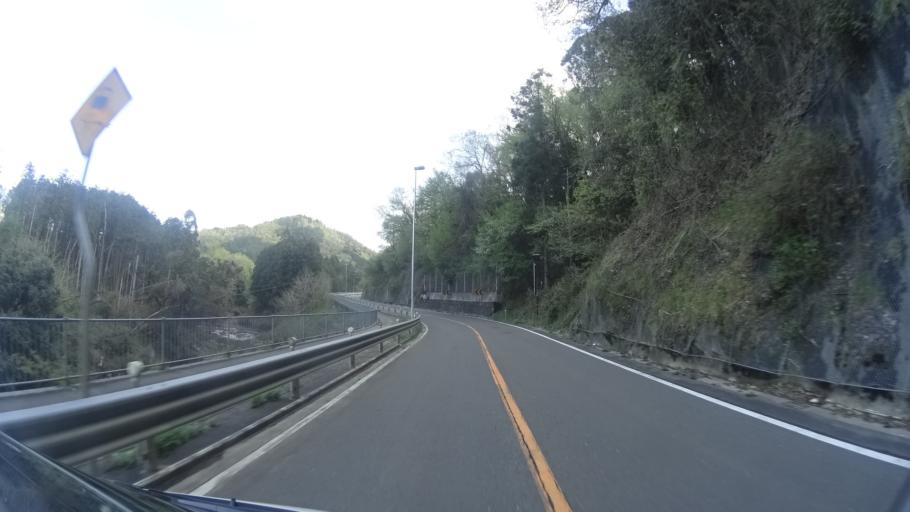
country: JP
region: Kyoto
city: Ayabe
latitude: 35.2025
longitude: 135.4218
